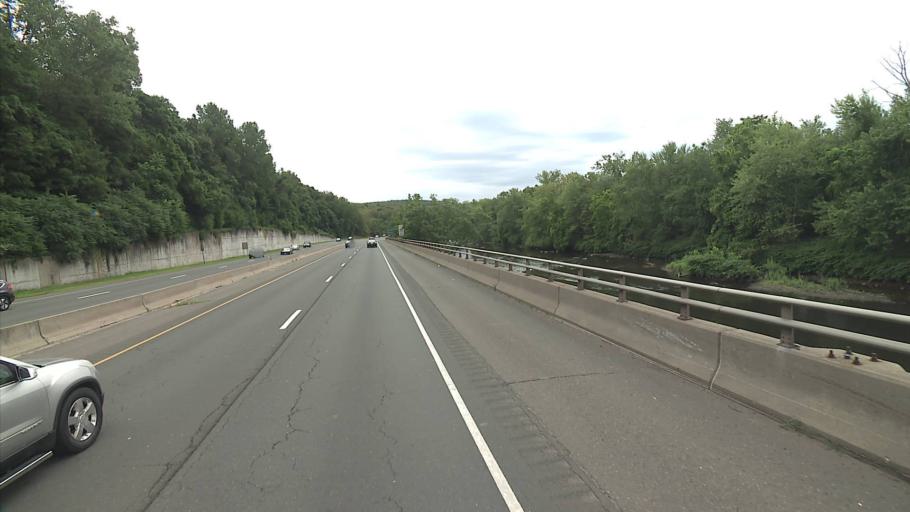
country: US
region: Connecticut
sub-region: New Haven County
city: Naugatuck
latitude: 41.4818
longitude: -73.0496
